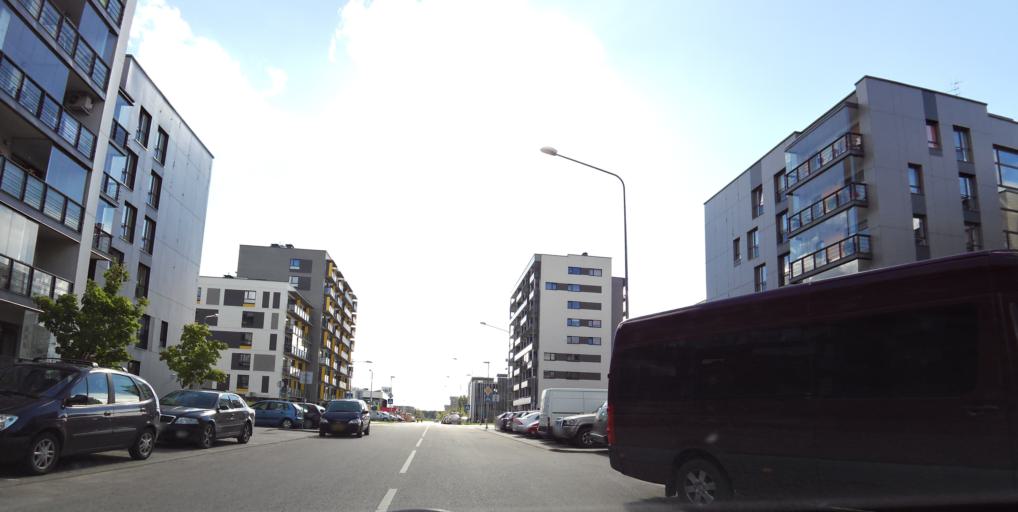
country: LT
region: Vilnius County
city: Pilaite
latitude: 54.7121
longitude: 25.1867
